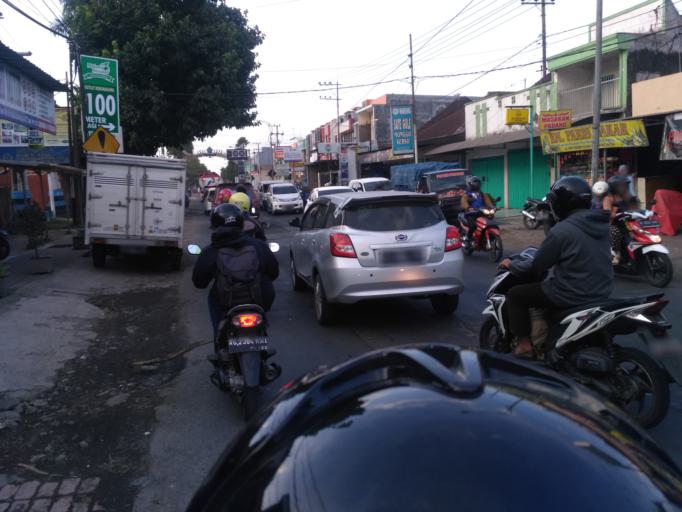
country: ID
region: East Java
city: Kebonsari
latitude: -8.0243
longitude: 112.6173
